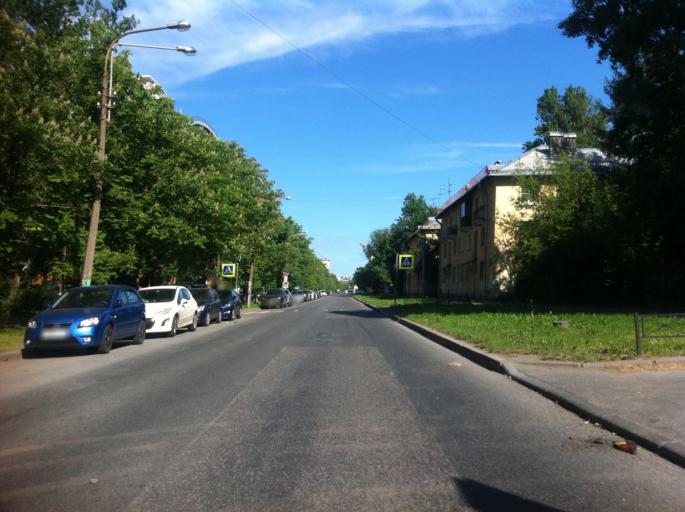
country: RU
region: St.-Petersburg
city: Dachnoye
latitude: 59.8375
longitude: 30.2521
